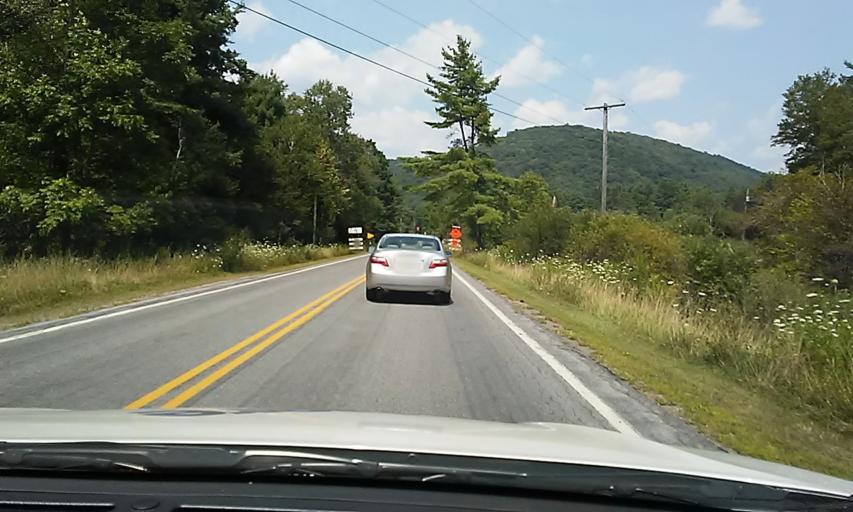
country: US
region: Pennsylvania
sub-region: Cameron County
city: Emporium
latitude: 41.5927
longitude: -78.1903
